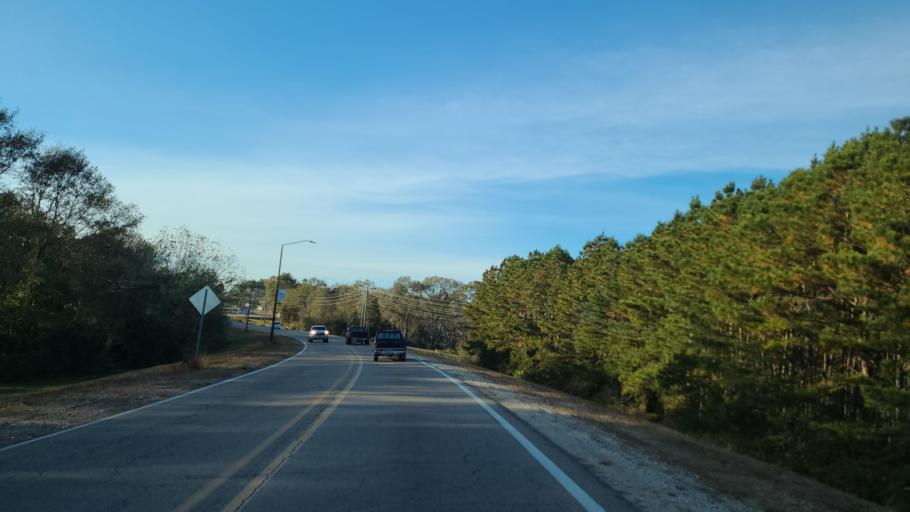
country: US
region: Mississippi
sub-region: Lamar County
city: Purvis
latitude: 31.1511
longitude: -89.4080
